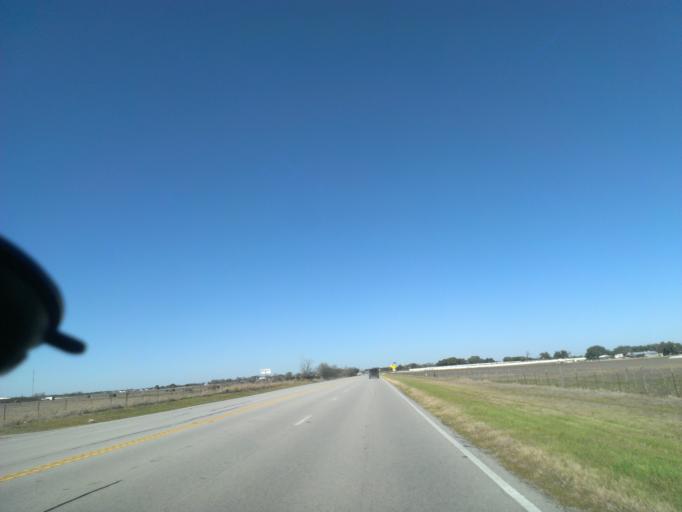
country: US
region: Texas
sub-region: Williamson County
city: Florence
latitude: 30.8753
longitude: -97.9177
